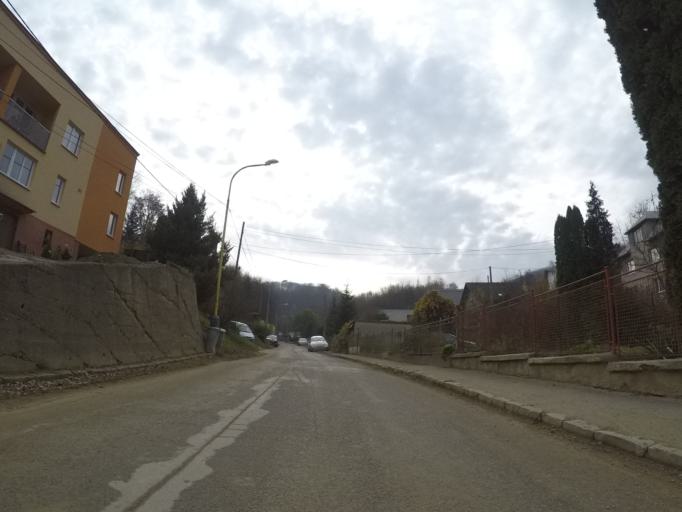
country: SK
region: Presovsky
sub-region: Okres Presov
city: Presov
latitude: 48.9823
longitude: 21.2170
